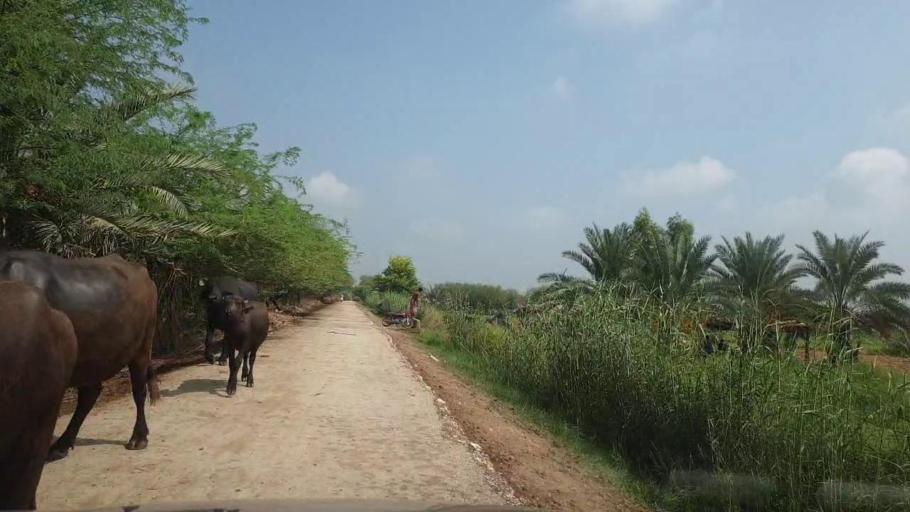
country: PK
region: Sindh
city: Pir jo Goth
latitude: 27.5970
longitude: 68.6940
